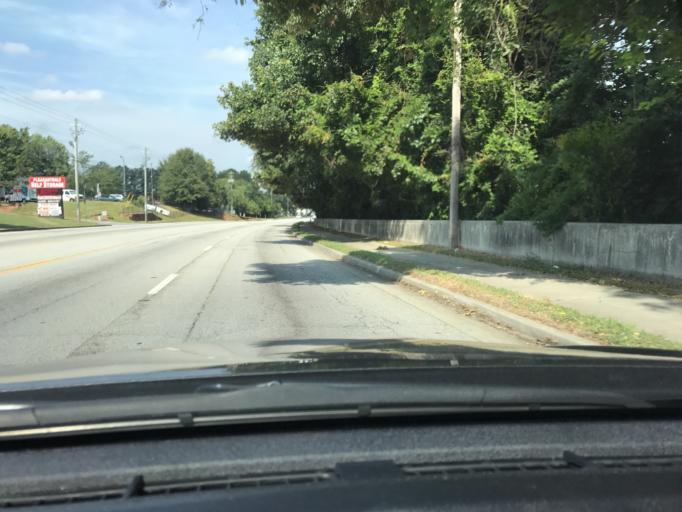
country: US
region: Georgia
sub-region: DeKalb County
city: Doraville
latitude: 33.8950
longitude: -84.2380
